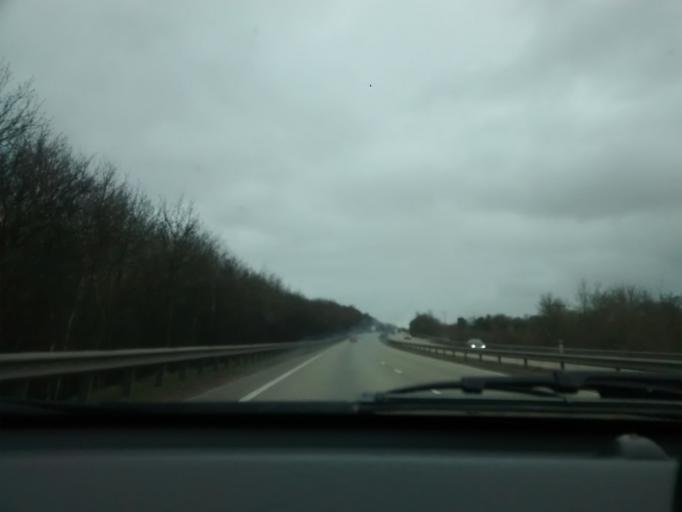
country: GB
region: England
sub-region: Suffolk
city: Bramford
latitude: 52.0754
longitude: 1.1113
